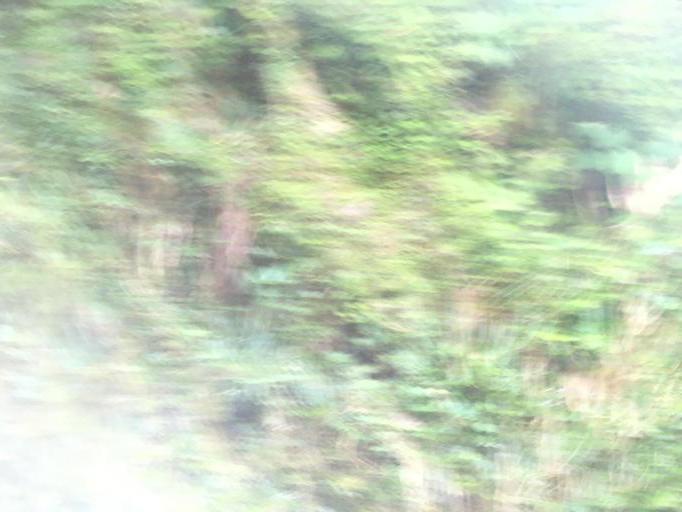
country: TW
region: Taiwan
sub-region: Yilan
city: Yilan
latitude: 24.6205
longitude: 121.4806
